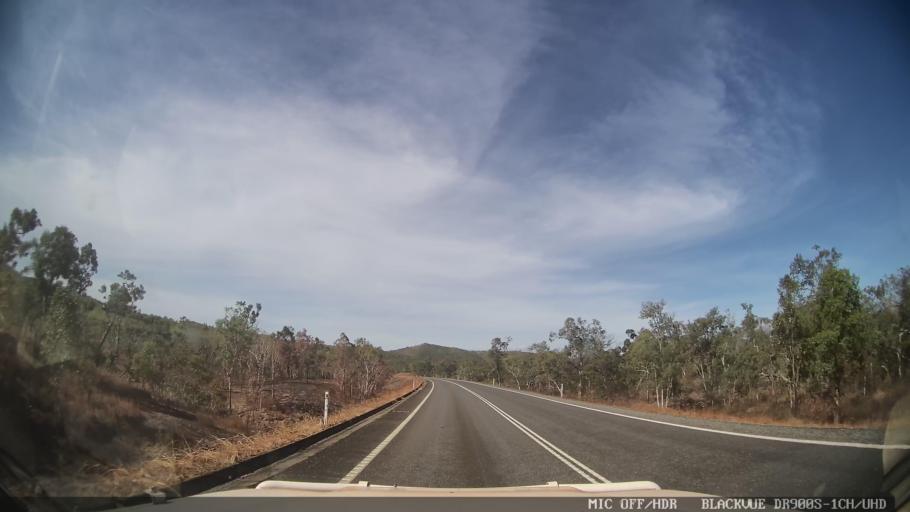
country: AU
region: Queensland
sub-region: Cook
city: Cooktown
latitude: -15.6788
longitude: 145.1737
